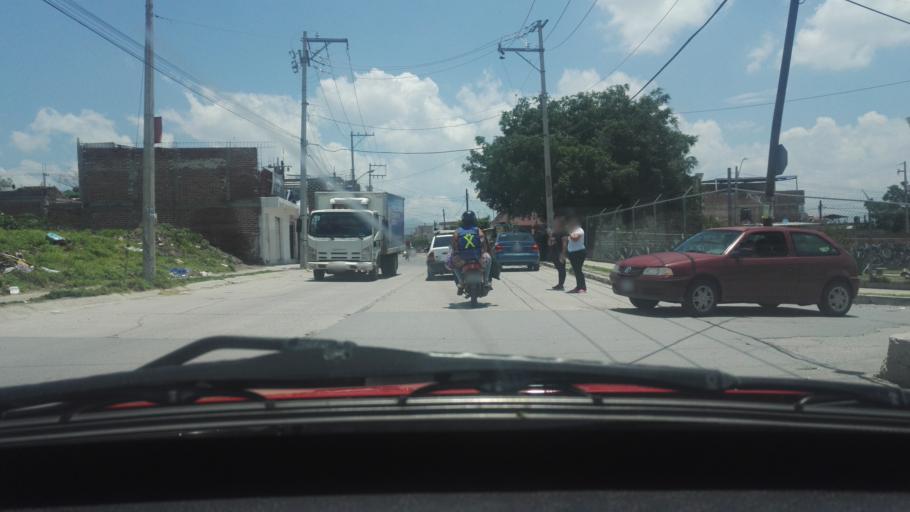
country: MX
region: Guanajuato
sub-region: Leon
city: San Jose de Duran (Los Troncoso)
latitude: 21.0825
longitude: -101.6329
